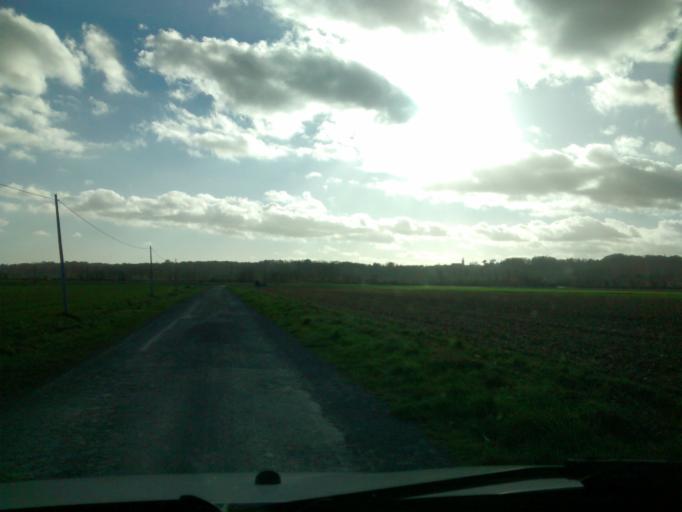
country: FR
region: Brittany
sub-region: Departement d'Ille-et-Vilaine
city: Roz-sur-Couesnon
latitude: 48.6044
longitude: -1.5822
